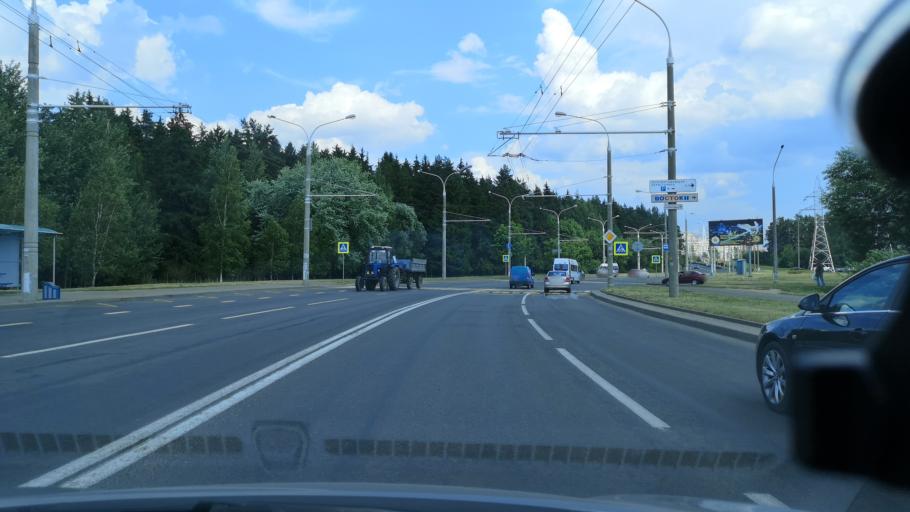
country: BY
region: Minsk
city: Borovlyany
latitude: 53.9443
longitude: 27.6567
